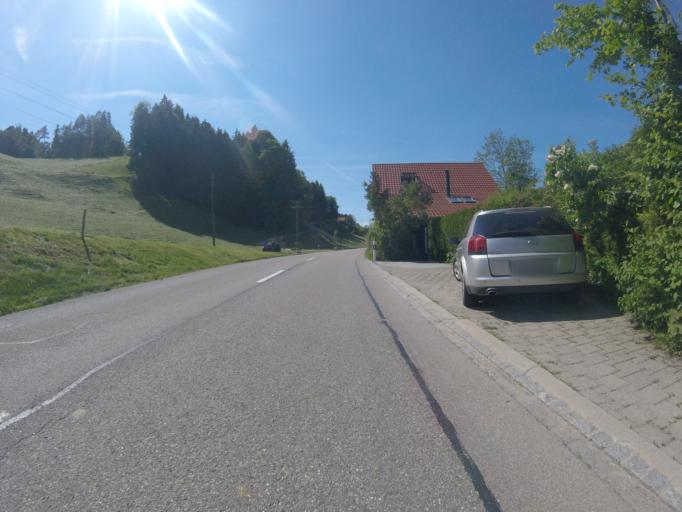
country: CH
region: Saint Gallen
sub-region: Wahlkreis Toggenburg
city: Oberhelfenschwil
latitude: 47.3772
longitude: 9.1166
